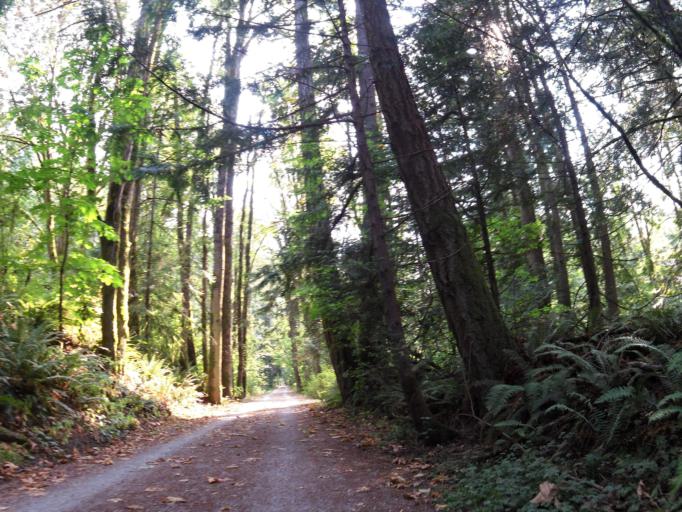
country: US
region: Washington
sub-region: Whatcom County
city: Bellingham
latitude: 48.7066
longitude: -122.4858
